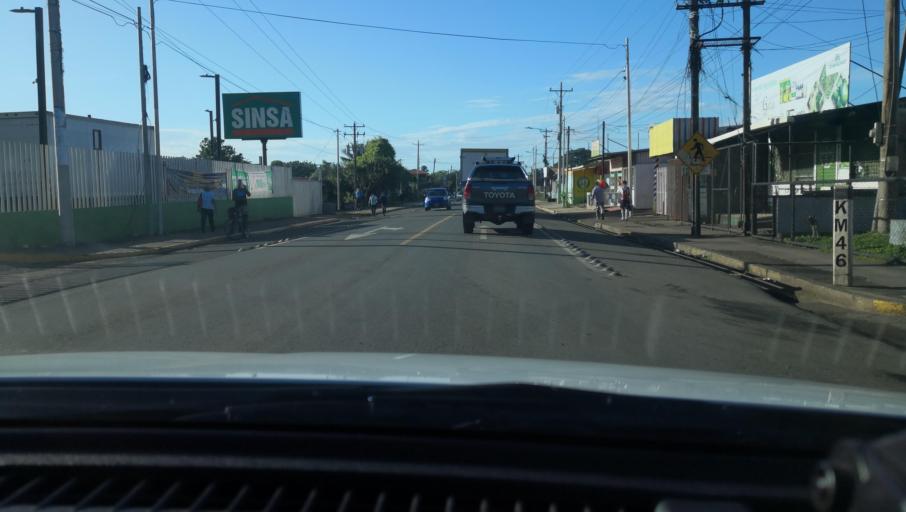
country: NI
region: Carazo
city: Jinotepe
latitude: 11.8493
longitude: -86.1945
